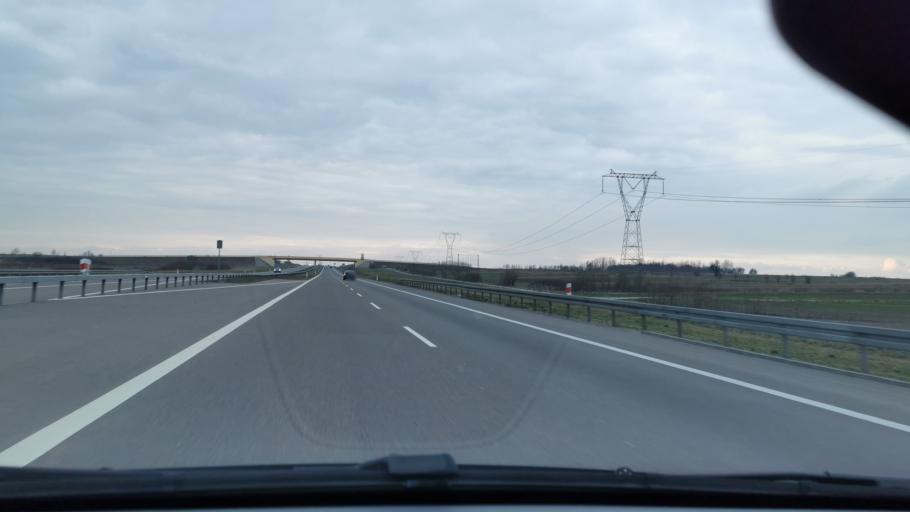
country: PL
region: Lublin Voivodeship
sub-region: Powiat pulawski
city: Markuszow
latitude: 51.3853
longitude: 22.2680
